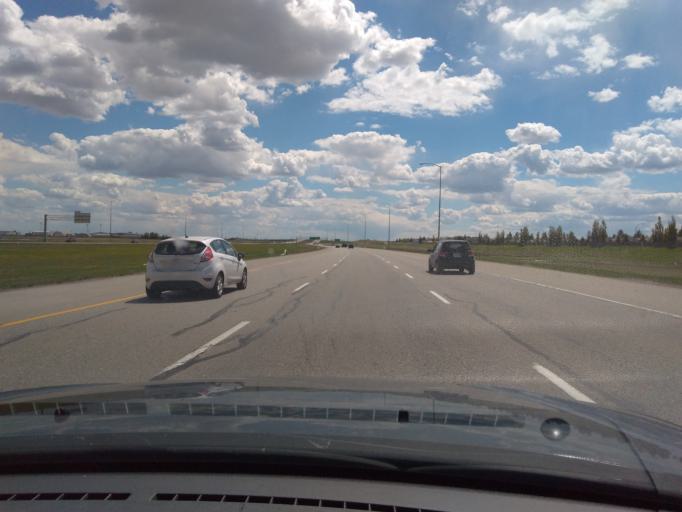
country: CA
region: Alberta
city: Chestermere
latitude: 51.0819
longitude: -113.9214
